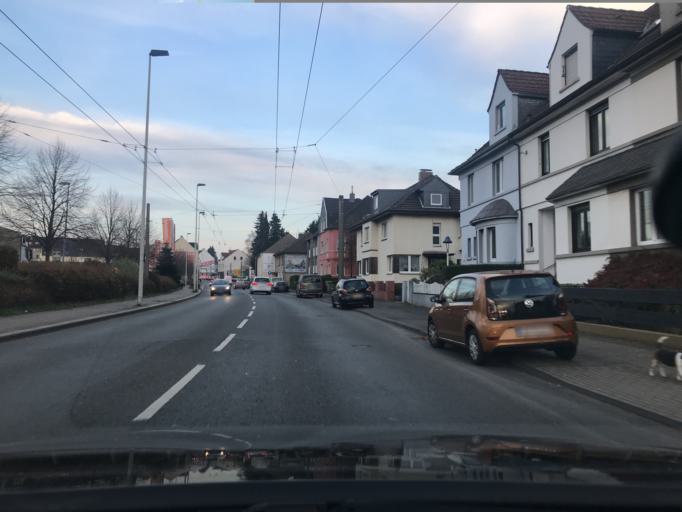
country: DE
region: North Rhine-Westphalia
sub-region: Regierungsbezirk Dusseldorf
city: Solingen
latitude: 51.1729
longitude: 7.0709
